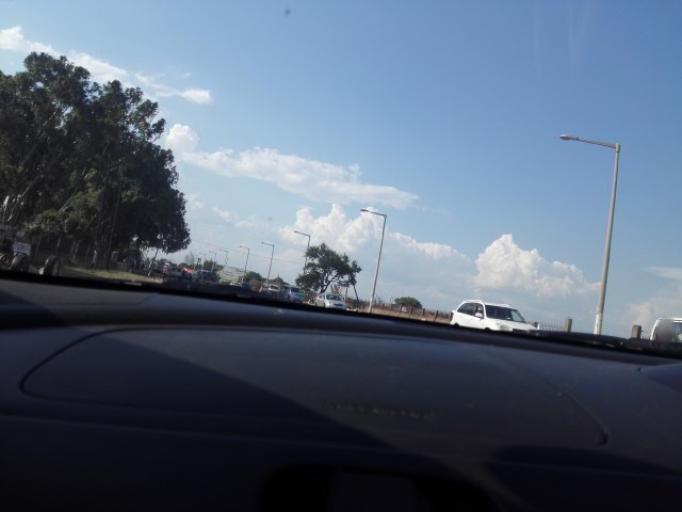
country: MZ
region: Maputo City
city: Maputo
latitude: -25.8804
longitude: 32.5680
